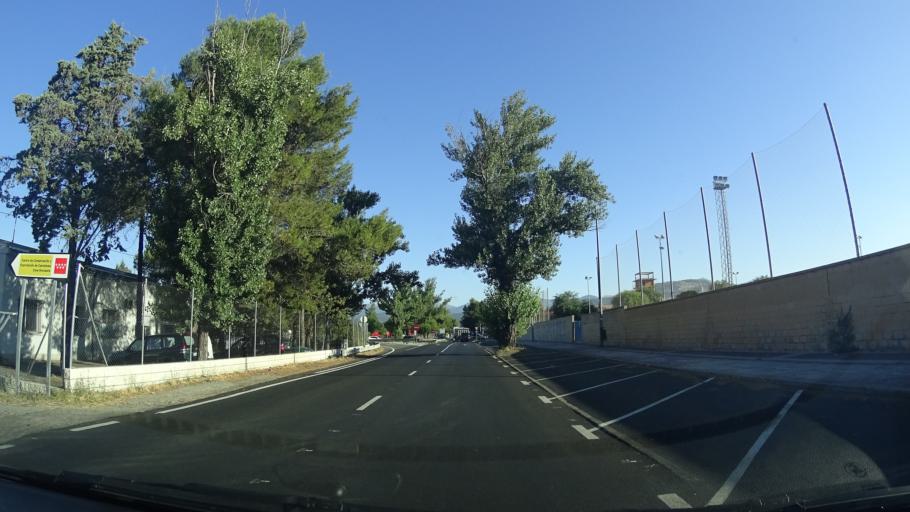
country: ES
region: Madrid
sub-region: Provincia de Madrid
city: Collado-Villalba
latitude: 40.6396
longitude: -4.0044
